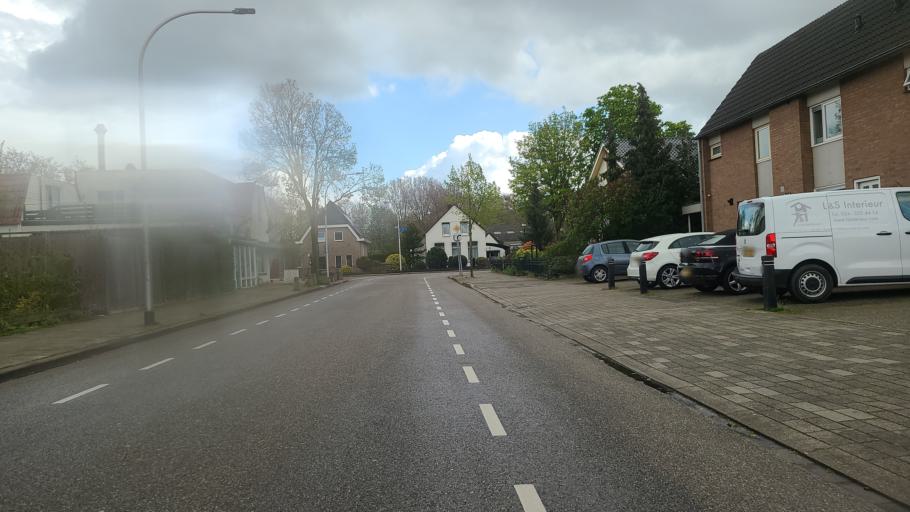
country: NL
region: Gelderland
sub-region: Gemeente Nijmegen
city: Lindenholt
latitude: 51.8321
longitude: 5.8039
